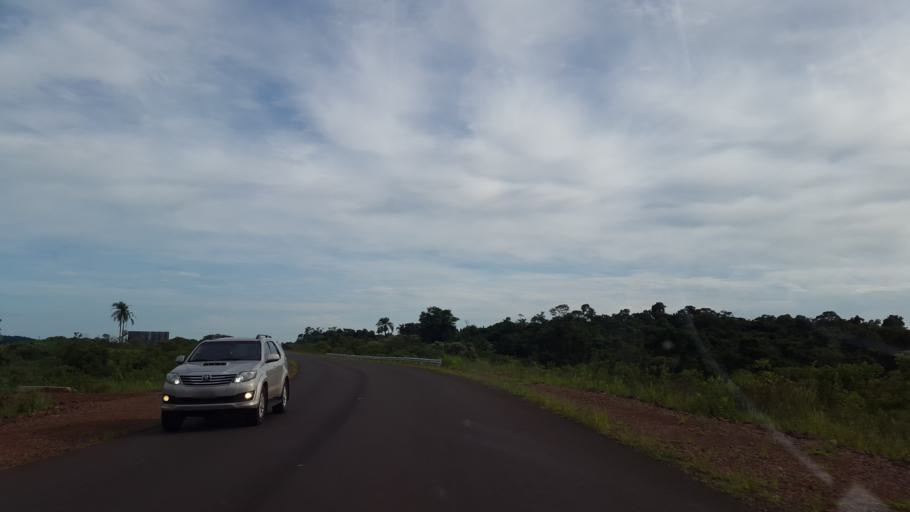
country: AR
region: Misiones
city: Bernardo de Irigoyen
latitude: -26.4155
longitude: -53.8236
